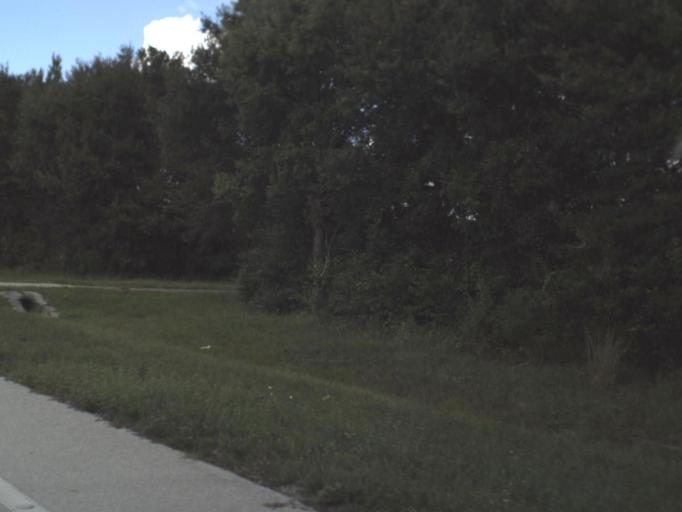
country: US
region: Florida
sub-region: DeSoto County
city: Southeast Arcadia
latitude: 27.2088
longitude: -81.7794
